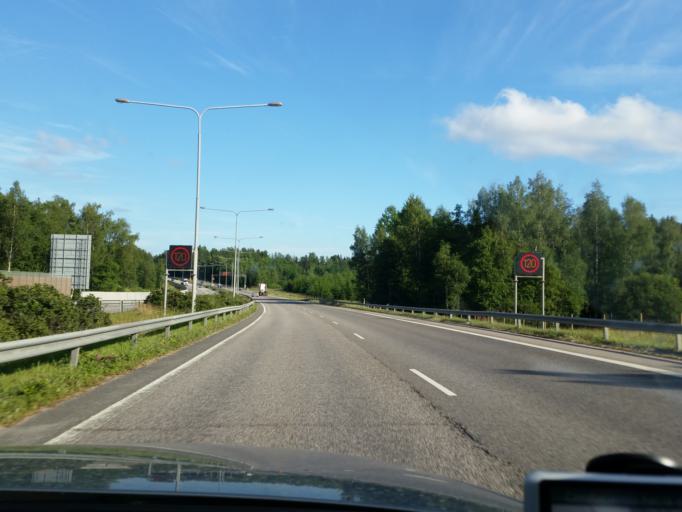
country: FI
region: Uusimaa
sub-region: Helsinki
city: Espoo
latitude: 60.2344
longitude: 24.5831
